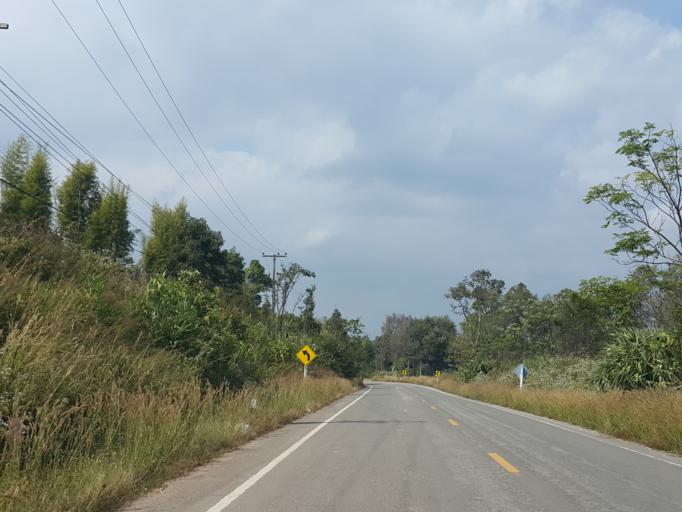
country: TH
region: Chiang Mai
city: Hot
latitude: 18.0951
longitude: 98.3713
